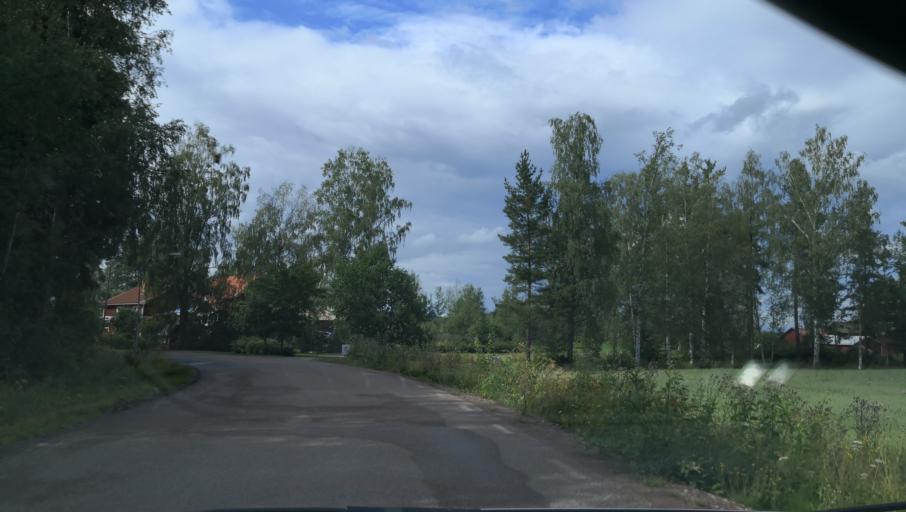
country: SE
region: Dalarna
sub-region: Borlange Kommun
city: Ornas
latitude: 60.4256
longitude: 15.6163
